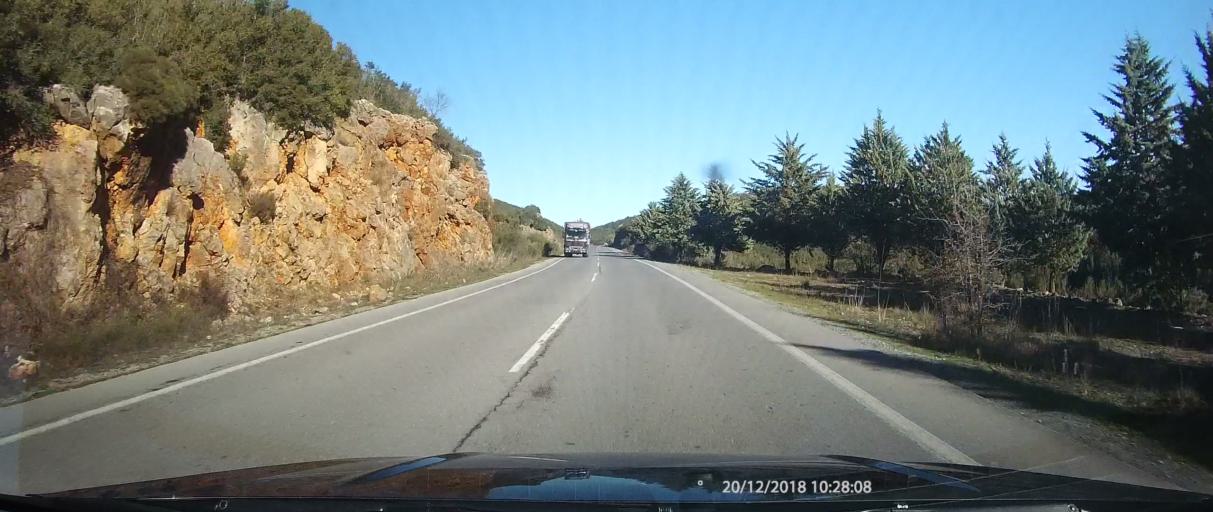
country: GR
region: Peloponnese
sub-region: Nomos Lakonias
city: Kariai
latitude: 37.2561
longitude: 22.4362
